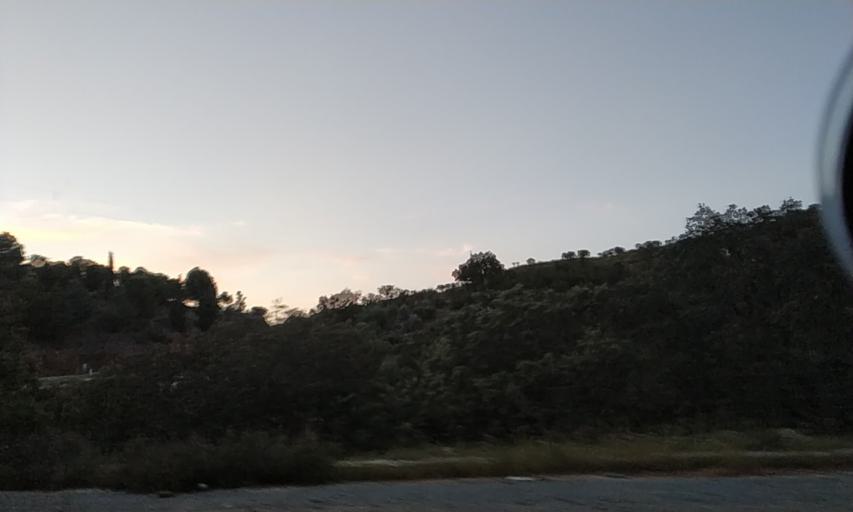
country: ES
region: Extremadura
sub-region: Provincia de Caceres
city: Alcantara
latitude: 39.7294
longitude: -6.8942
